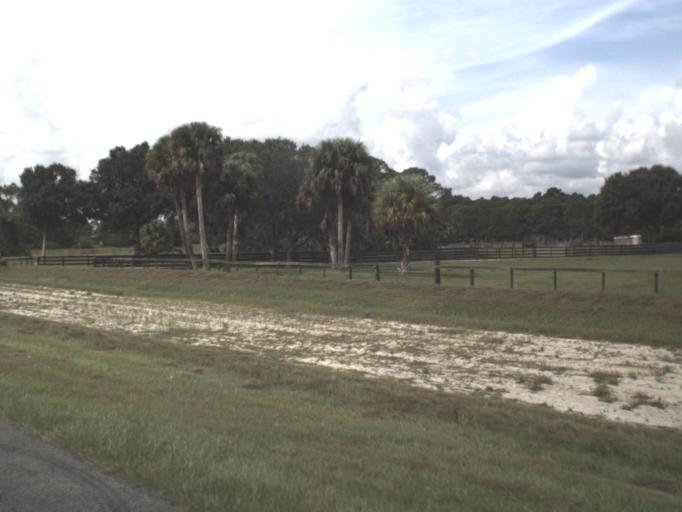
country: US
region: Florida
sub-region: Okeechobee County
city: Taylor Creek
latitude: 27.3016
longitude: -80.6787
